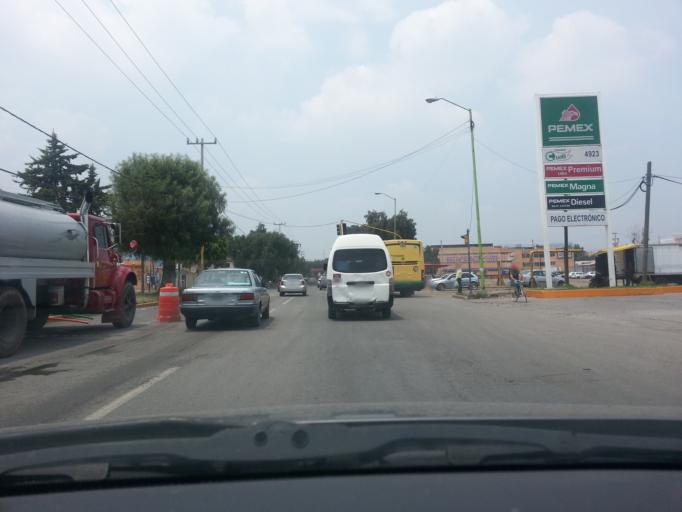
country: MX
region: Mexico
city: Cuautitlan Izcalli
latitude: 19.6675
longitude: -99.2118
